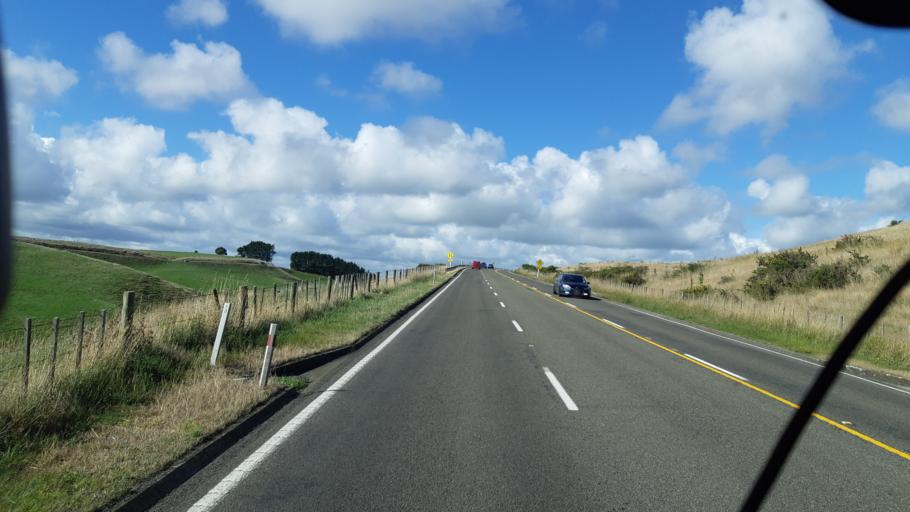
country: NZ
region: Manawatu-Wanganui
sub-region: Wanganui District
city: Wanganui
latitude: -40.0252
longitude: 175.1863
